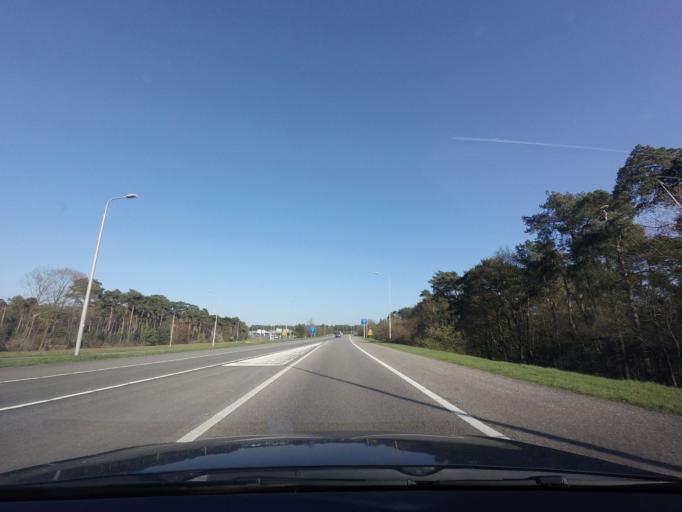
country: NL
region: Utrecht
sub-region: Gemeente Amersfoort
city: Amersfoort
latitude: 52.1323
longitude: 5.3767
